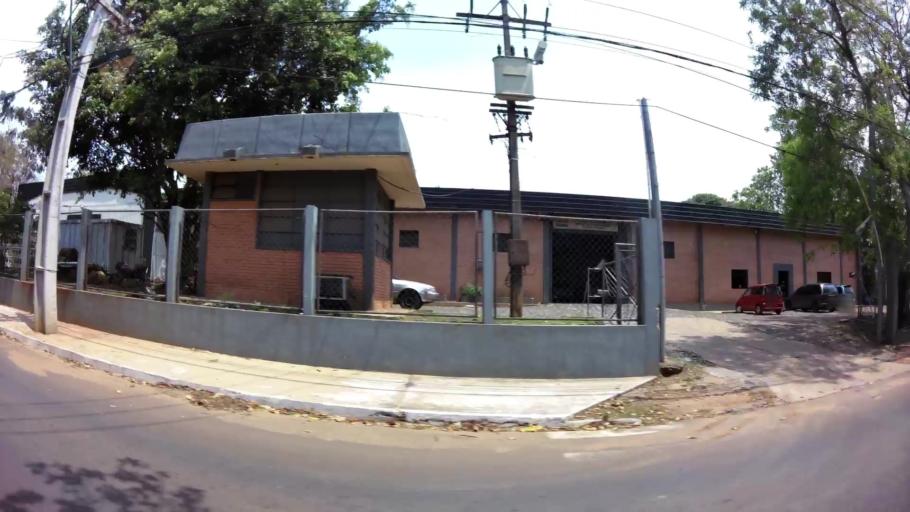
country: PY
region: Central
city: Fernando de la Mora
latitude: -25.3086
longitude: -57.5653
